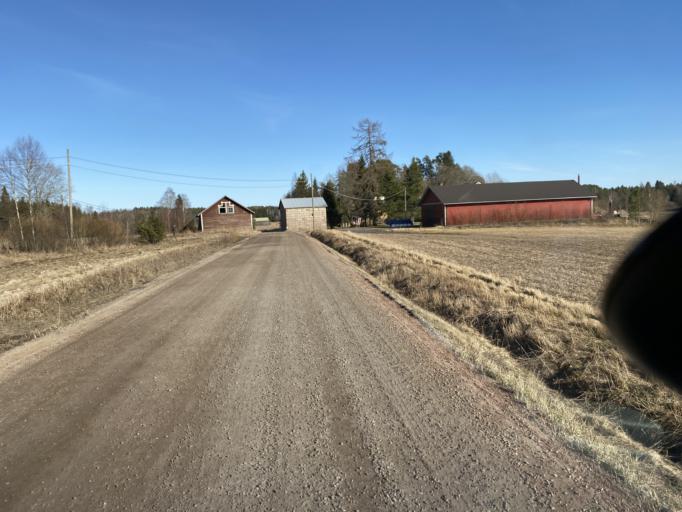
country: FI
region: Satakunta
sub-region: Rauma
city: Lappi
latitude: 61.1409
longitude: 21.9395
